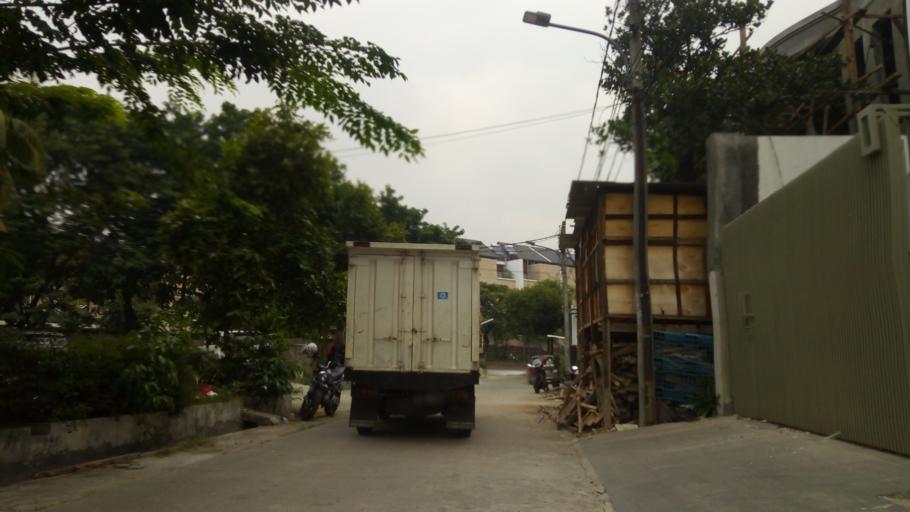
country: ID
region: Jakarta Raya
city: Jakarta
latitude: -6.1498
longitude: 106.8410
